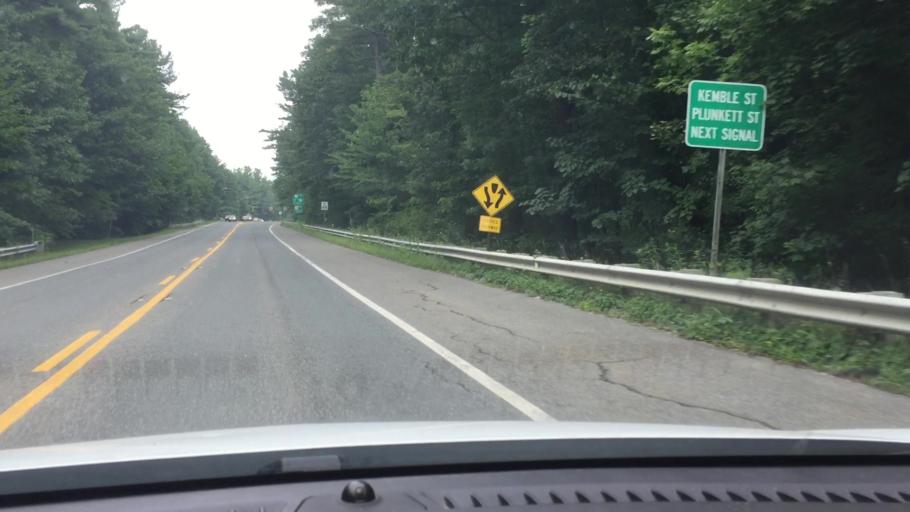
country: US
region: Massachusetts
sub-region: Berkshire County
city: Lenox
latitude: 42.3330
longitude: -73.2858
